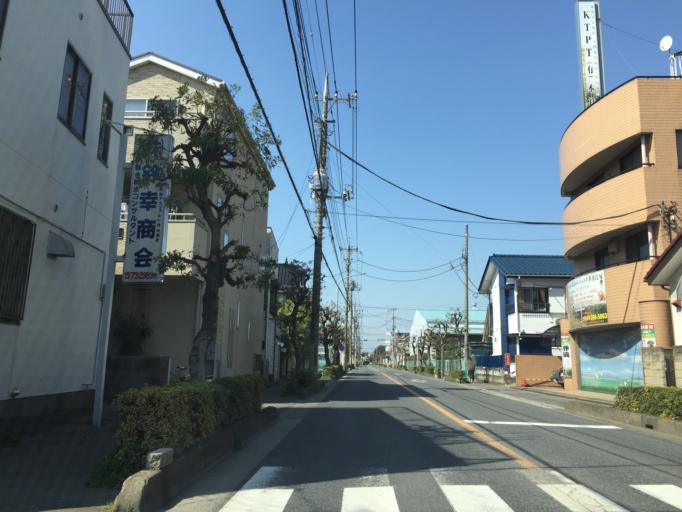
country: JP
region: Saitama
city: Shiki
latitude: 35.8416
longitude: 139.5924
